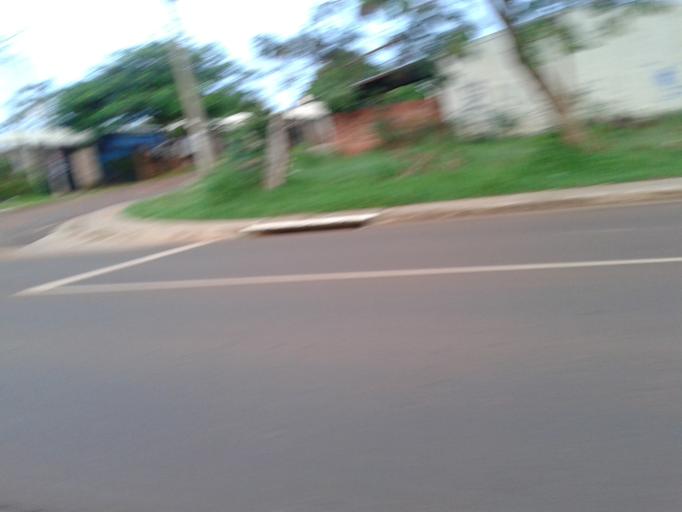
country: AR
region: Misiones
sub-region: Departamento de Capital
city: Posadas
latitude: -27.3943
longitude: -55.9498
